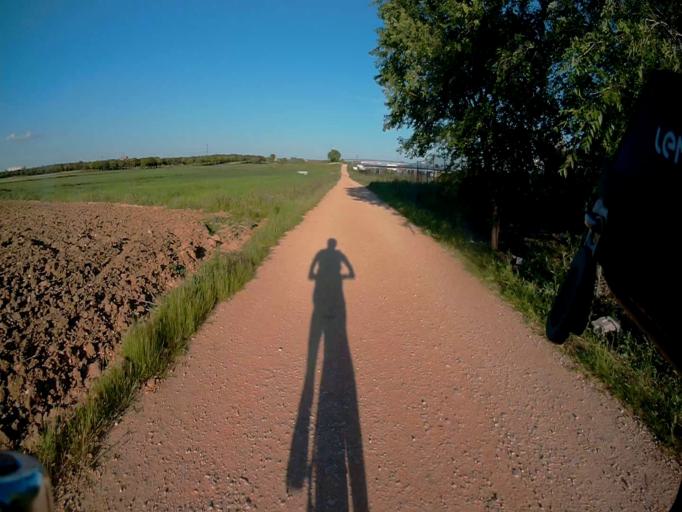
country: ES
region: Madrid
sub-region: Provincia de Madrid
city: Fuenlabrada
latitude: 40.3138
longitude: -3.8073
